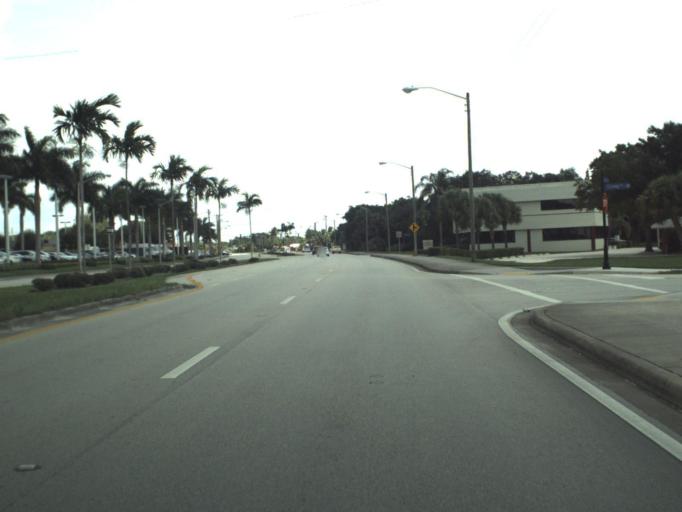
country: US
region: Florida
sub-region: Palm Beach County
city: North Palm Beach
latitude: 26.8110
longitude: -80.0772
